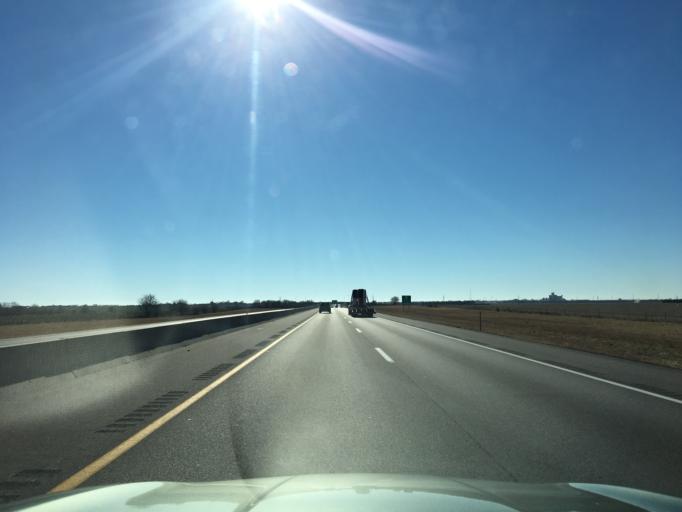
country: US
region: Kansas
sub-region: Sumner County
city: Wellington
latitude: 37.2964
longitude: -97.3404
